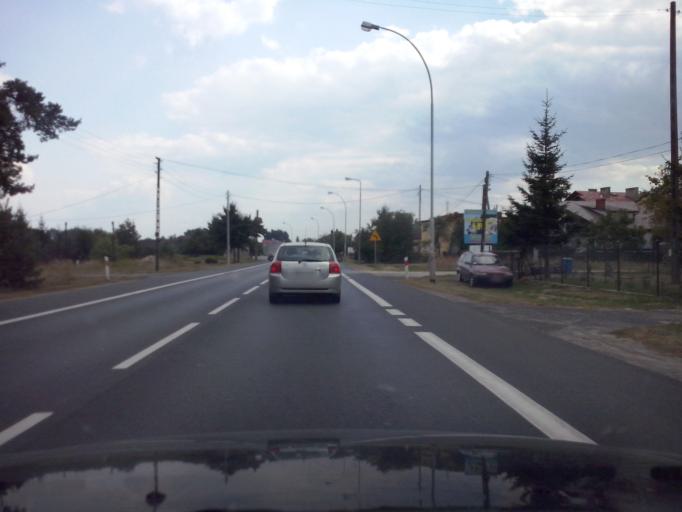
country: PL
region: Subcarpathian Voivodeship
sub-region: Powiat nizanski
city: Nisko
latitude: 50.5310
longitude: 22.1076
